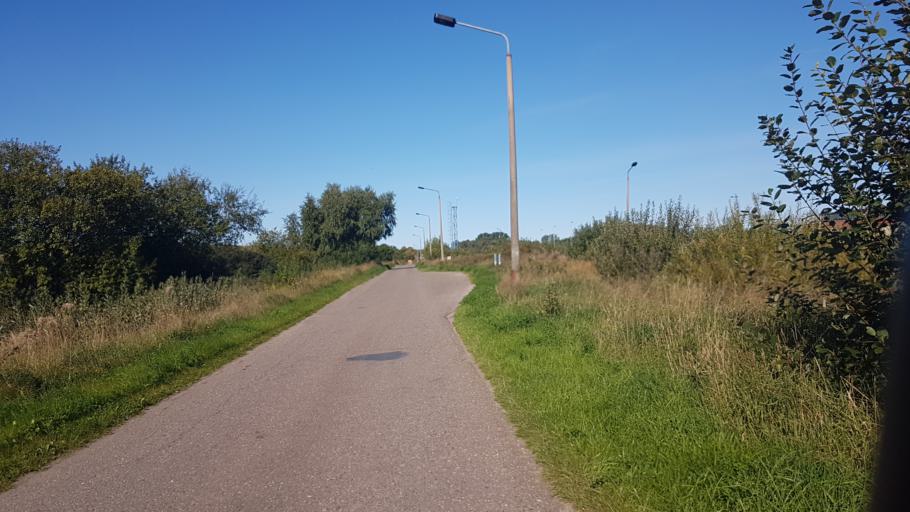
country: DE
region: Mecklenburg-Vorpommern
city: Sagard
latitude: 54.4979
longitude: 13.5453
